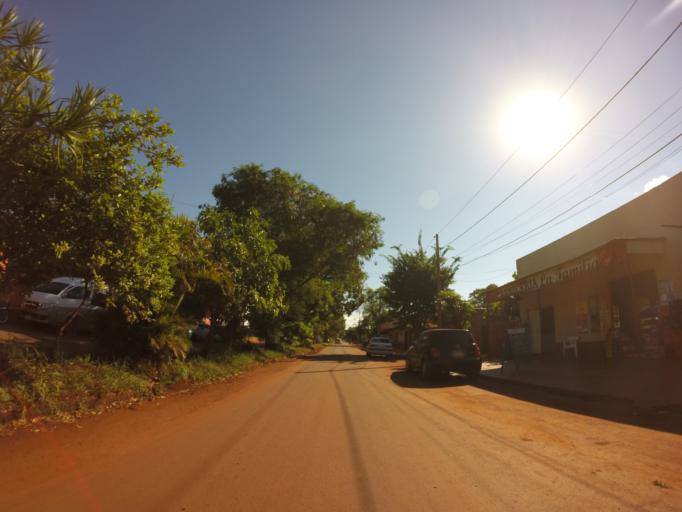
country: PY
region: Alto Parana
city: Ciudad del Este
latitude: -25.3764
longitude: -54.6479
